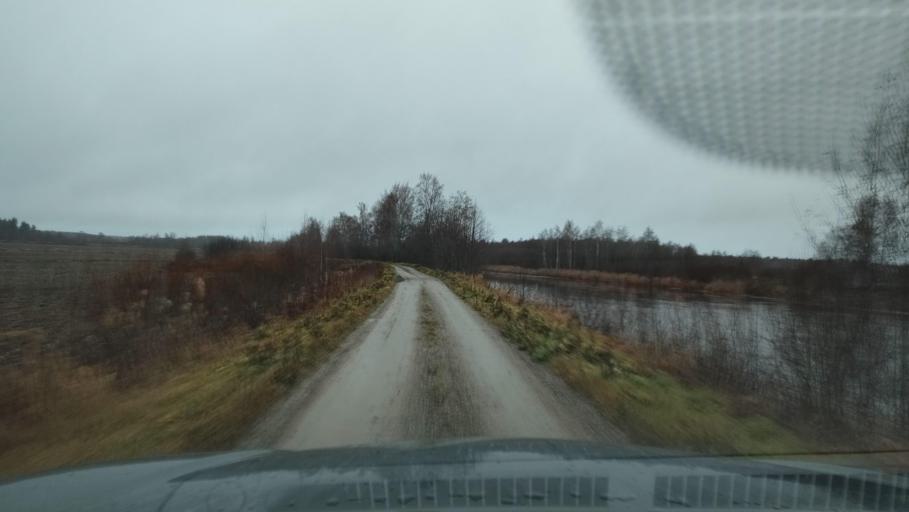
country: FI
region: Ostrobothnia
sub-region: Sydosterbotten
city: Kristinestad
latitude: 62.2324
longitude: 21.4534
